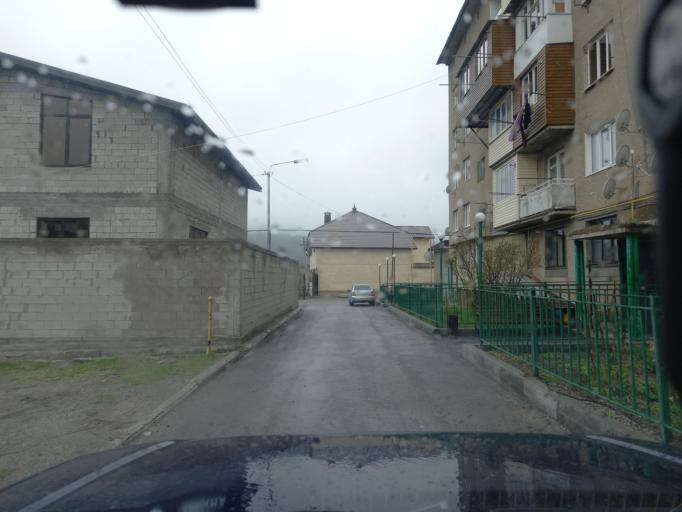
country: RU
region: Kabardino-Balkariya
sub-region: El'brusskiy Rayon
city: El'brus
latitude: 43.2570
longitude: 42.6435
